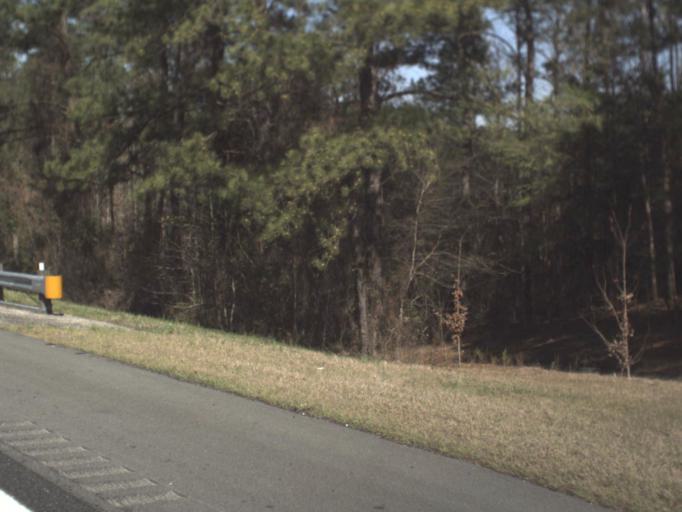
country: US
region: Florida
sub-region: Gadsden County
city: Chattahoochee
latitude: 30.6207
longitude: -84.8376
